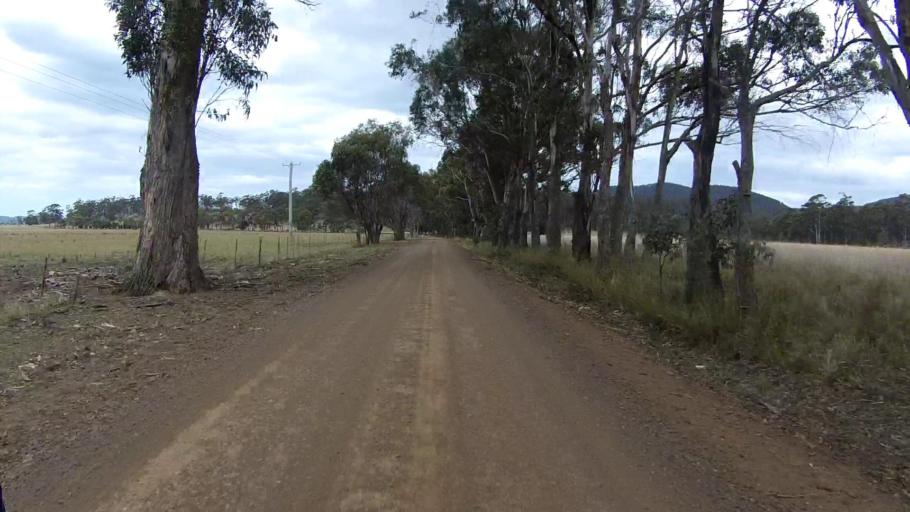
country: AU
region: Tasmania
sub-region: Sorell
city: Sorell
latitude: -42.6532
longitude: 147.9136
